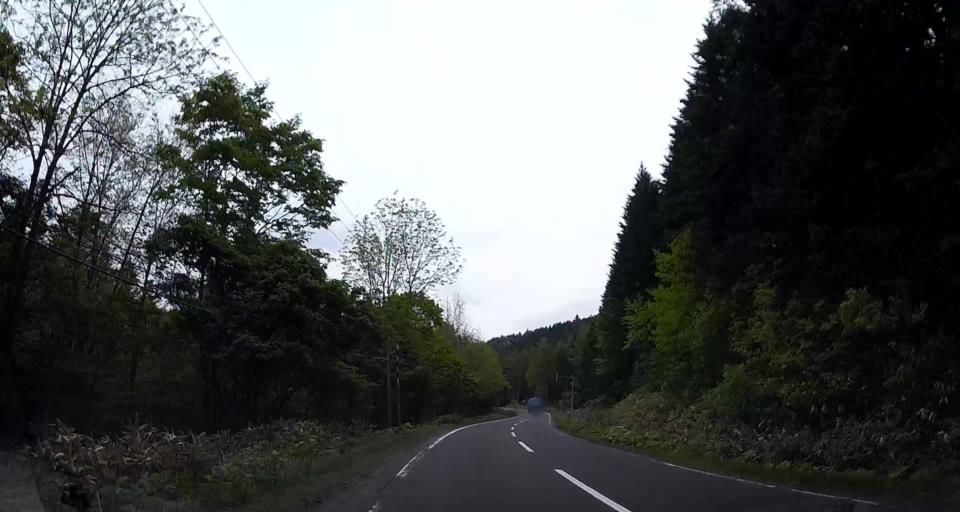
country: JP
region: Hokkaido
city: Shiraoi
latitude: 42.6817
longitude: 141.0998
